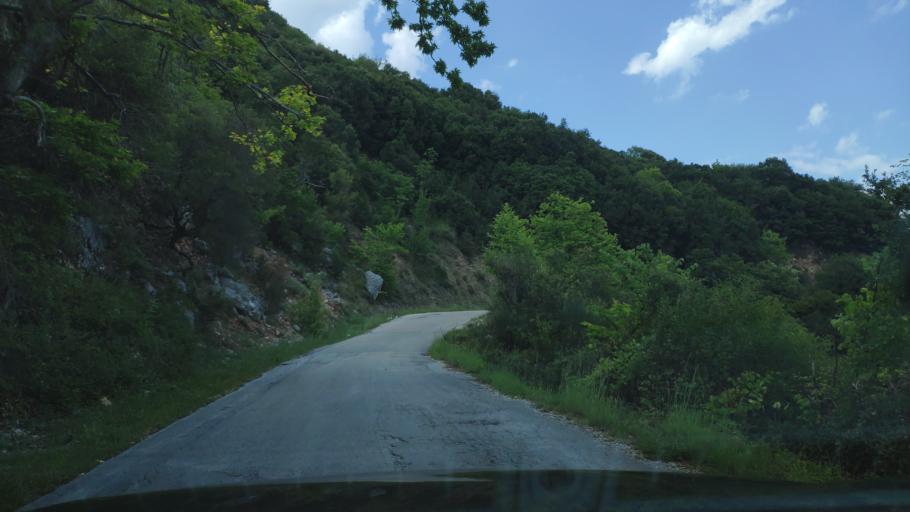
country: GR
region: Epirus
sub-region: Nomos Artas
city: Agios Dimitrios
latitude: 39.4519
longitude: 21.0205
